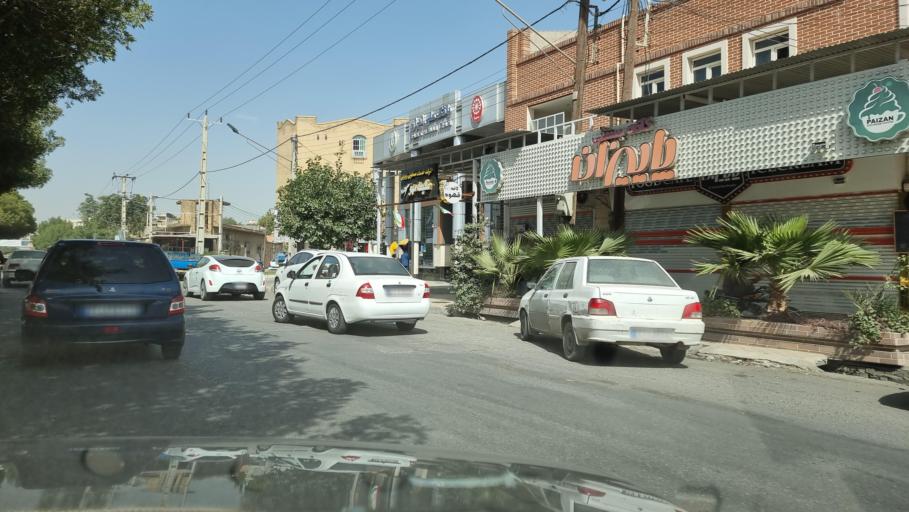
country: IR
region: Khuzestan
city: Dezful
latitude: 32.3854
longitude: 48.4124
